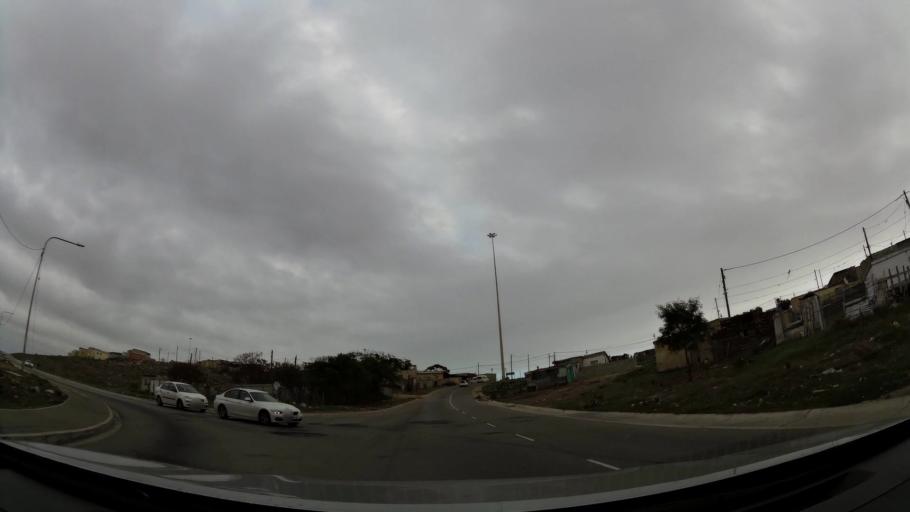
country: ZA
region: Eastern Cape
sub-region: Nelson Mandela Bay Metropolitan Municipality
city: Port Elizabeth
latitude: -33.9116
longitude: 25.5397
